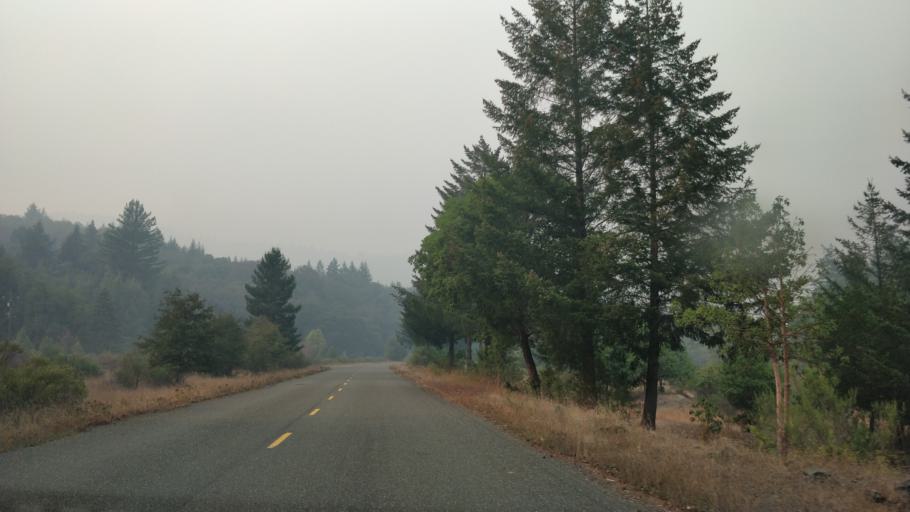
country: US
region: California
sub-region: Humboldt County
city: Rio Dell
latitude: 40.3352
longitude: -124.0263
